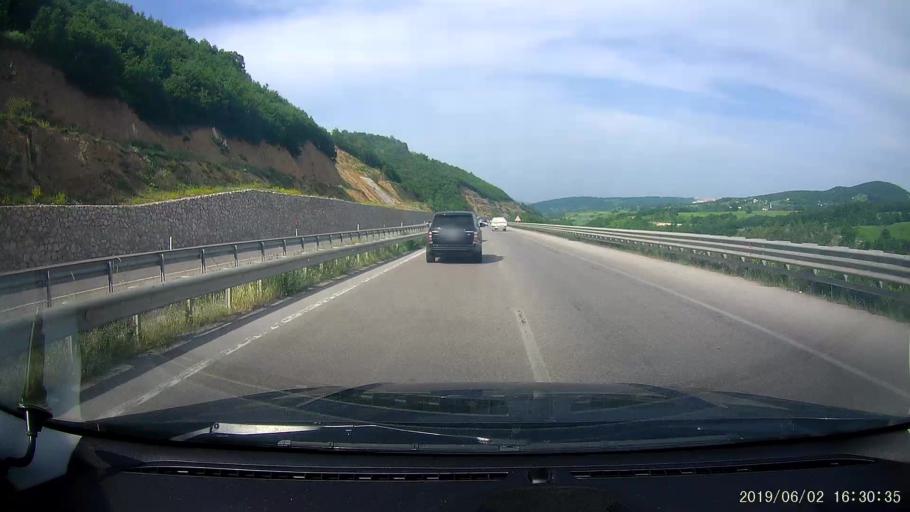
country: TR
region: Samsun
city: Ladik
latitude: 41.0264
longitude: 35.8854
